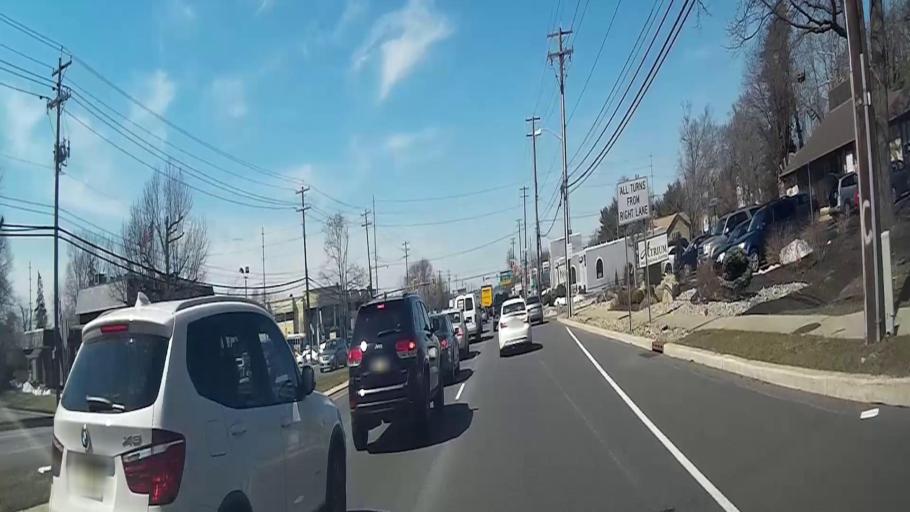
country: US
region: New Jersey
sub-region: Camden County
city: Springdale
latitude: 39.9024
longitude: -74.9653
